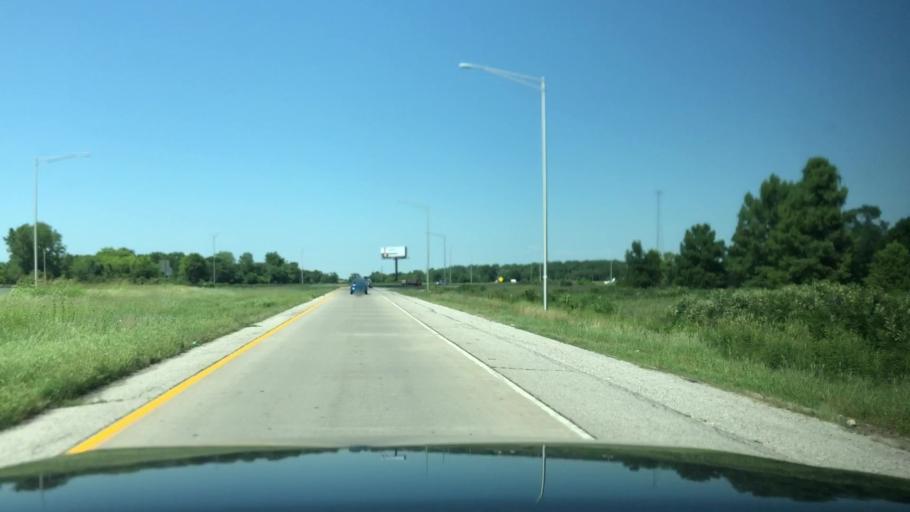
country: US
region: Illinois
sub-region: Saint Clair County
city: Alorton
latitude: 38.5820
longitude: -90.1050
